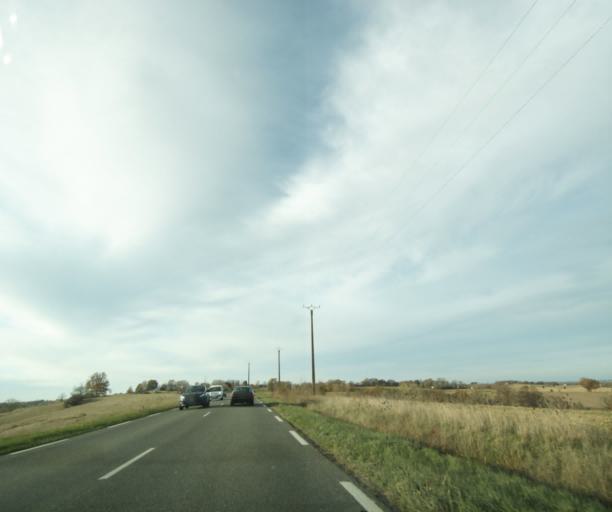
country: FR
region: Midi-Pyrenees
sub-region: Departement du Gers
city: Eauze
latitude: 43.7854
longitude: 0.1104
